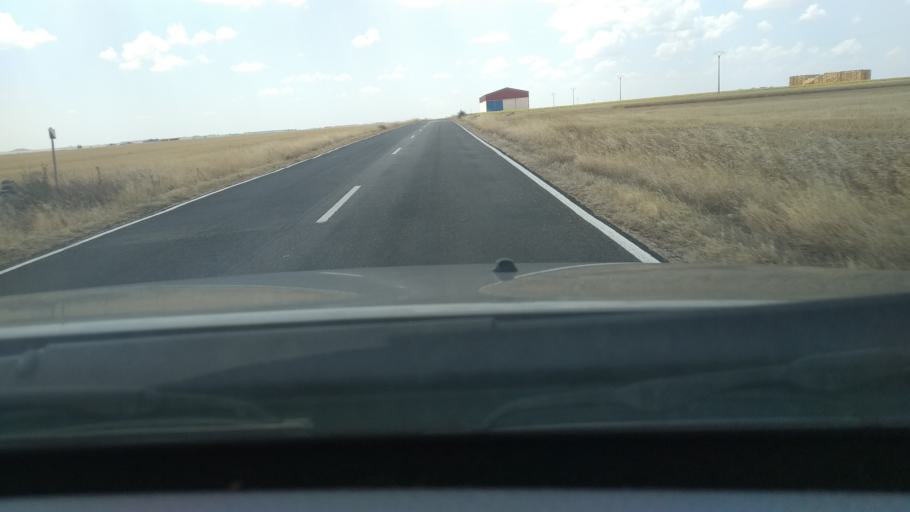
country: ES
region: Castille and Leon
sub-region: Provincia de Burgos
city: Villafruela
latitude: 41.9315
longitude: -3.8863
